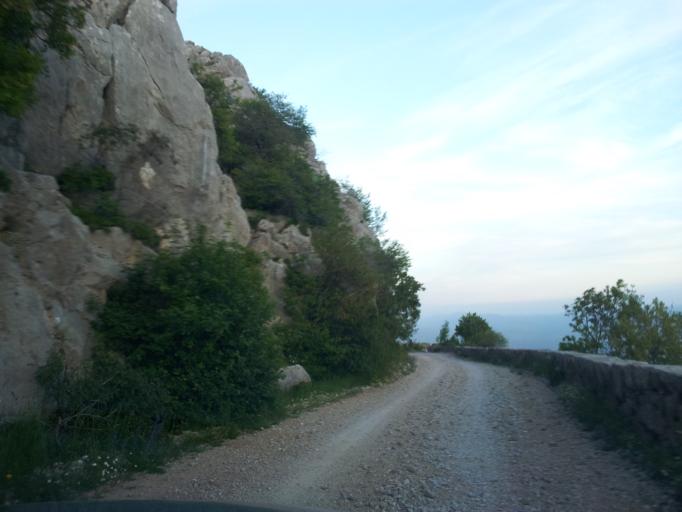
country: HR
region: Zadarska
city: Obrovac
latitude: 44.2611
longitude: 15.6489
